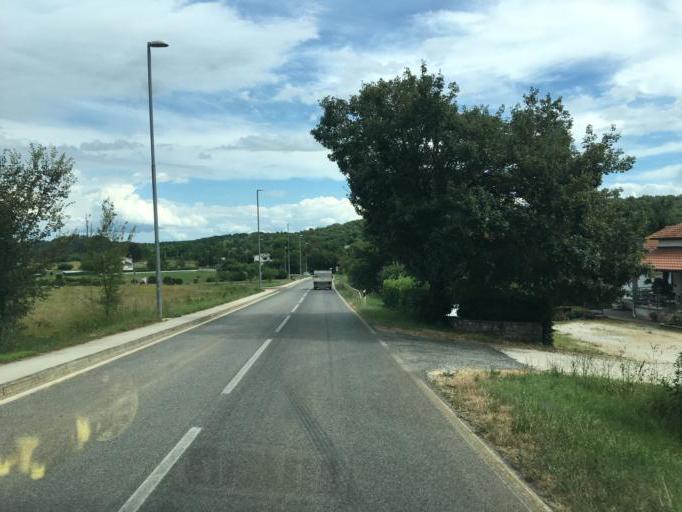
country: HR
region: Istarska
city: Karojba
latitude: 45.2779
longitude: 13.8464
